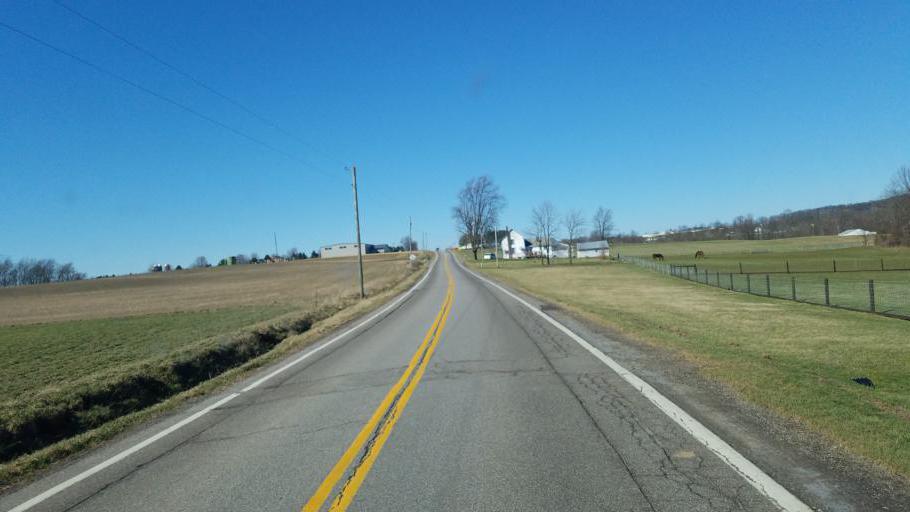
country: US
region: Ohio
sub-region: Wayne County
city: Dalton
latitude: 40.7267
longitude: -81.6953
